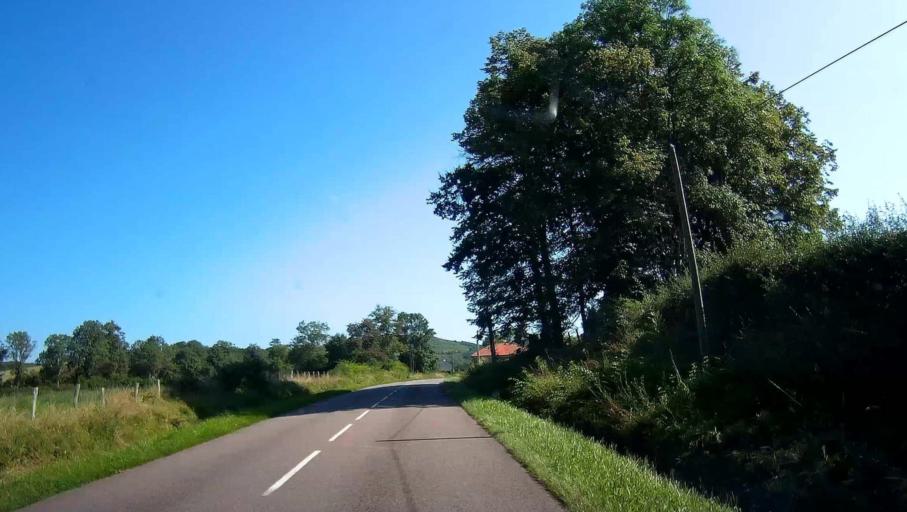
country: FR
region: Bourgogne
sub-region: Departement de la Cote-d'Or
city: Nolay
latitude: 46.9124
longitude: 4.5983
